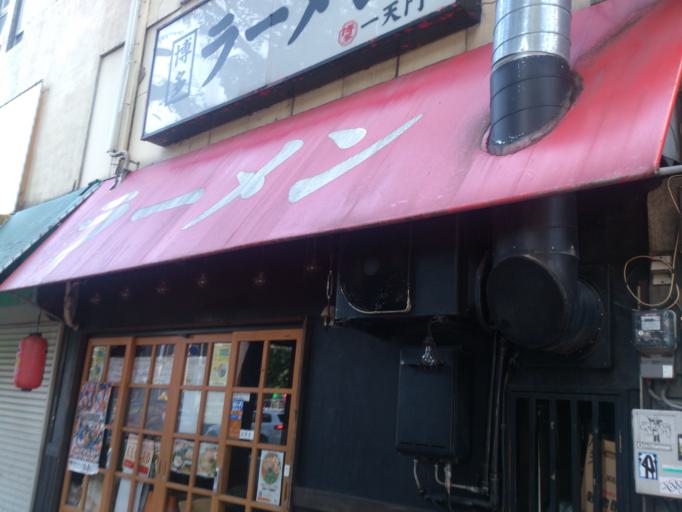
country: JP
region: Fukuoka
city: Fukuoka-shi
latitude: 33.5923
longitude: 130.4113
